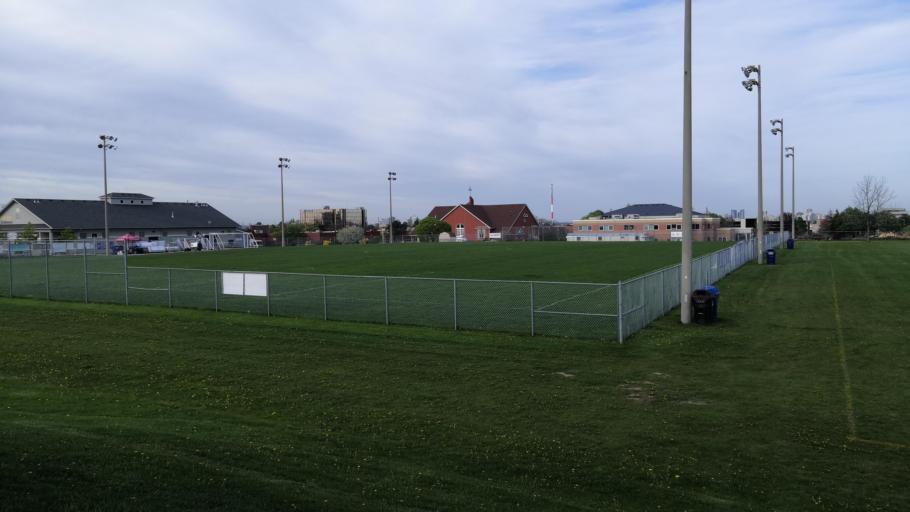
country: CA
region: Ontario
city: Concord
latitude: 43.7795
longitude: -79.4921
